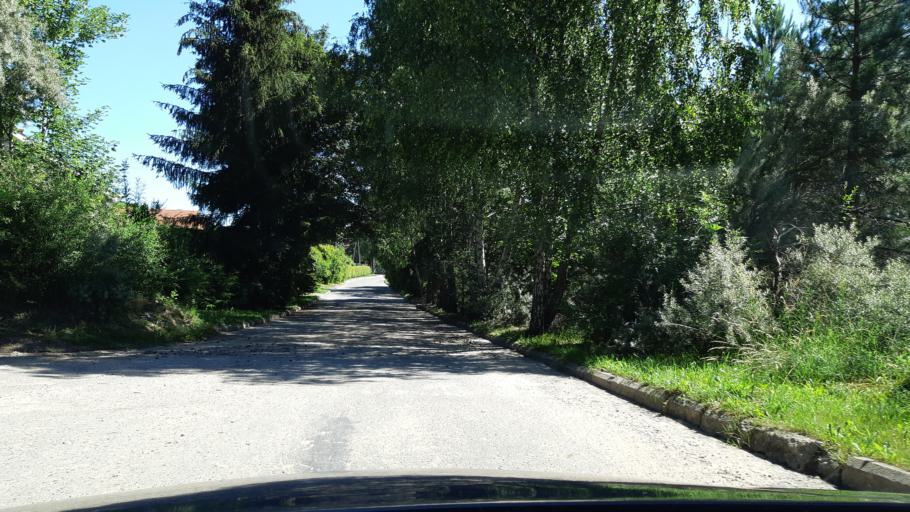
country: PL
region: Warmian-Masurian Voivodeship
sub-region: Powiat mragowski
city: Mragowo
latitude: 53.8462
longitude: 21.2998
